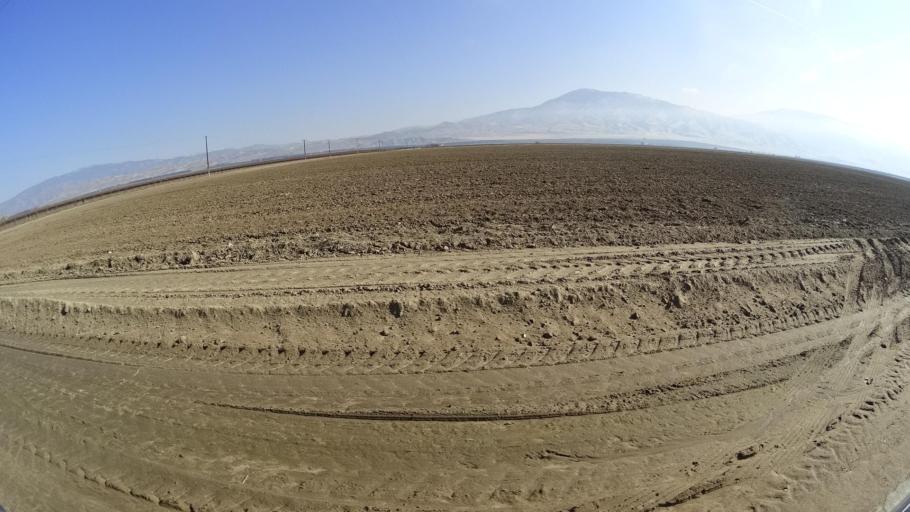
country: US
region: California
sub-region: Kern County
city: Arvin
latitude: 35.2522
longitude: -118.8069
